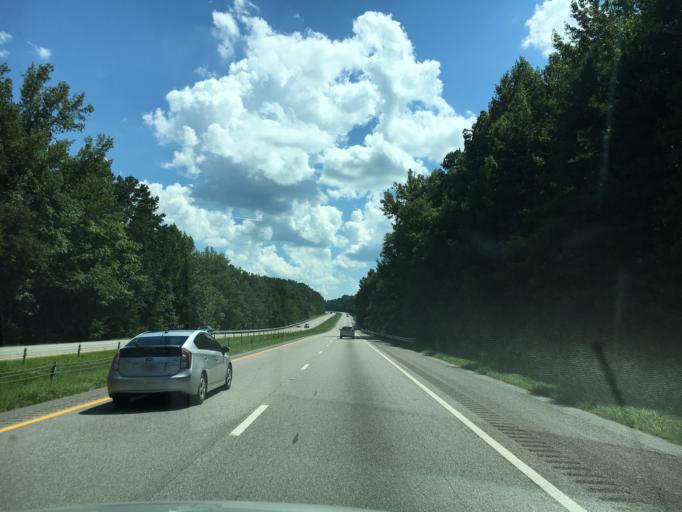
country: US
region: South Carolina
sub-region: Laurens County
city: Clinton
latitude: 34.5885
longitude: -81.8926
